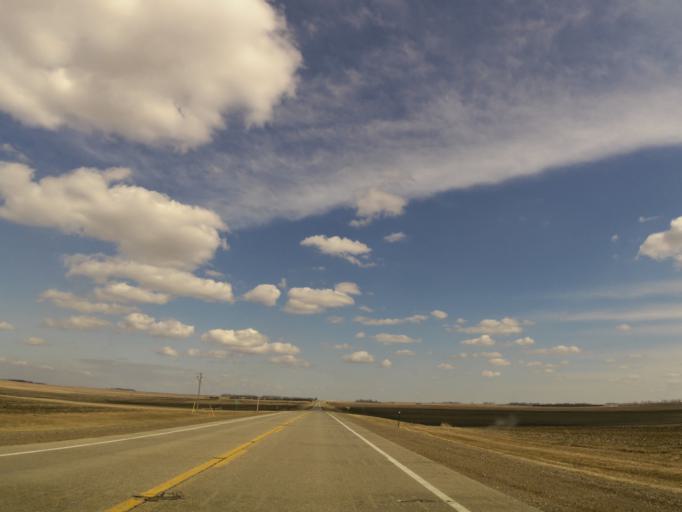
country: US
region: South Dakota
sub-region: Deuel County
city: Clear Lake
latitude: 44.8901
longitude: -96.8029
